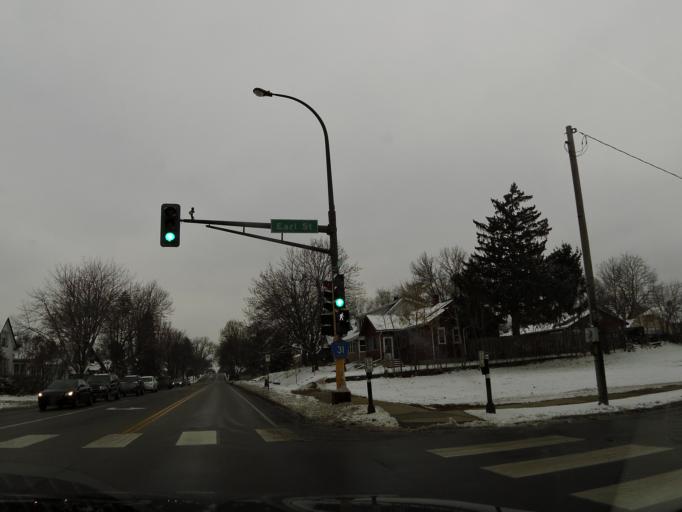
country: US
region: Minnesota
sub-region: Ramsey County
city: Saint Paul
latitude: 44.9776
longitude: -93.0558
